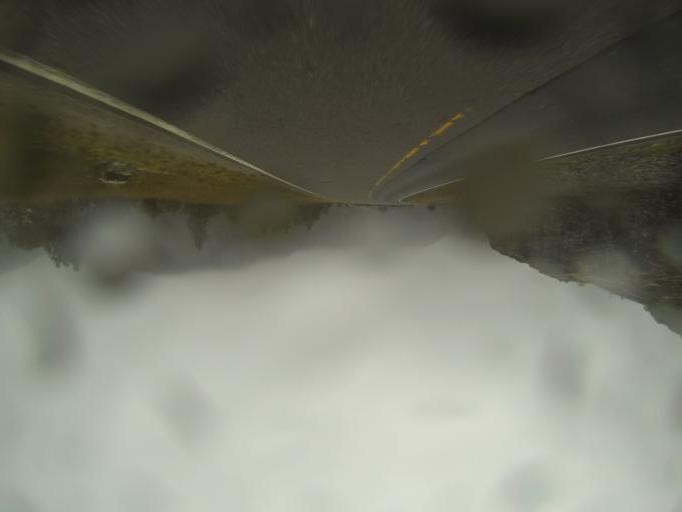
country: NO
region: Vest-Agder
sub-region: Sirdal
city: Tonstad
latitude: 58.9134
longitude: 6.7463
